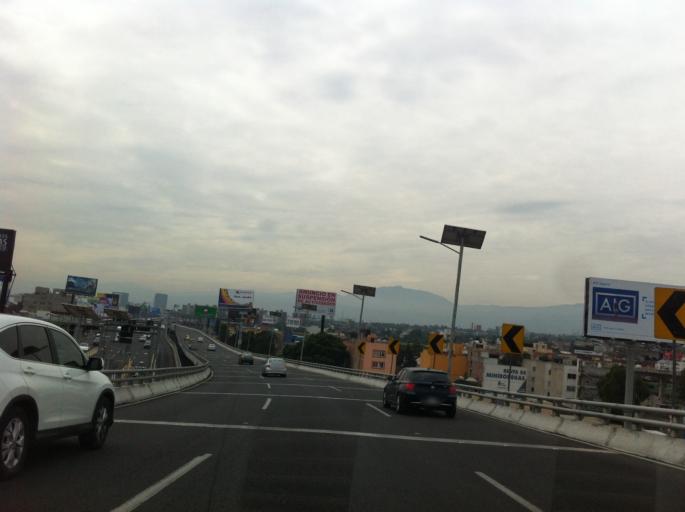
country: MX
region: Mexico City
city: Alvaro Obregon
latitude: 19.3830
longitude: -99.1912
